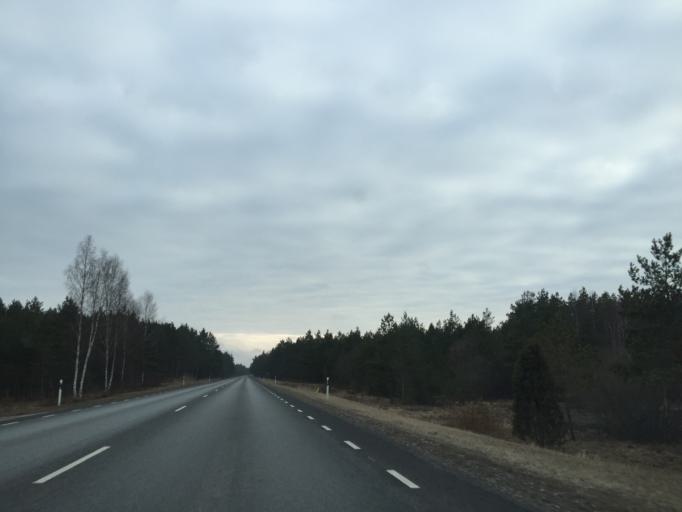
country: EE
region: Saare
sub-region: Orissaare vald
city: Orissaare
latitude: 58.5067
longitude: 22.8694
